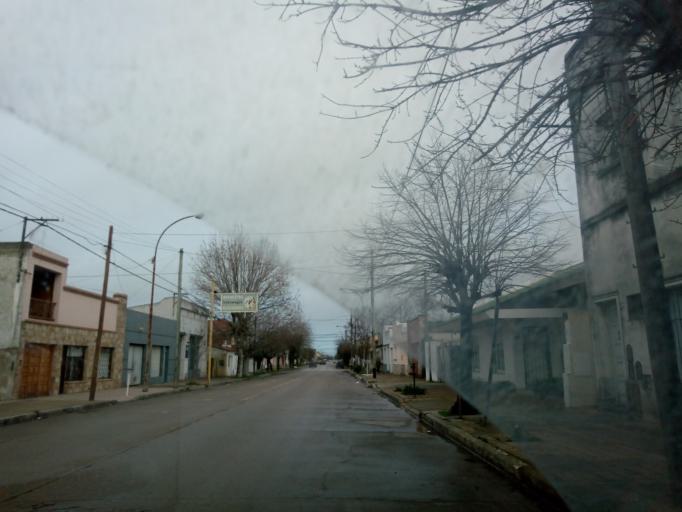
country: AR
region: Buenos Aires
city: Necochea
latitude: -38.5600
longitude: -58.7345
